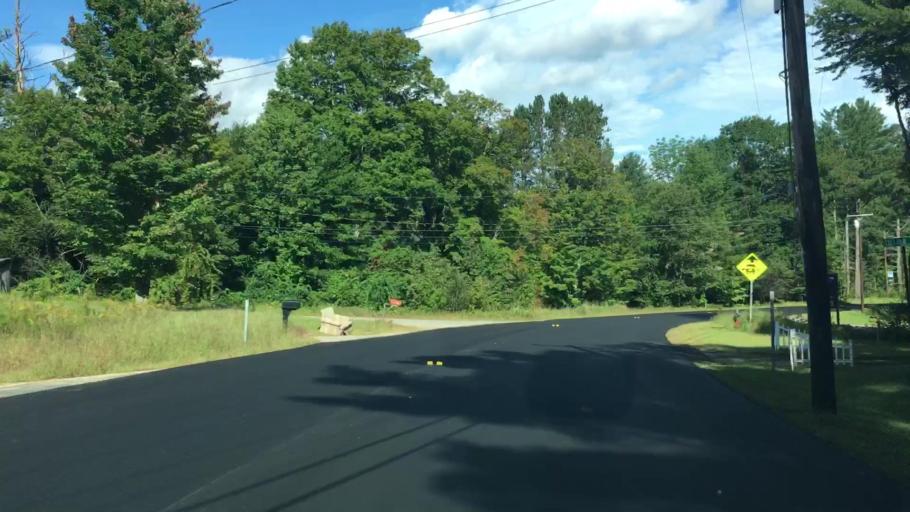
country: US
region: New Hampshire
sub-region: Grafton County
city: Woodstock
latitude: 44.0326
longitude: -71.6991
